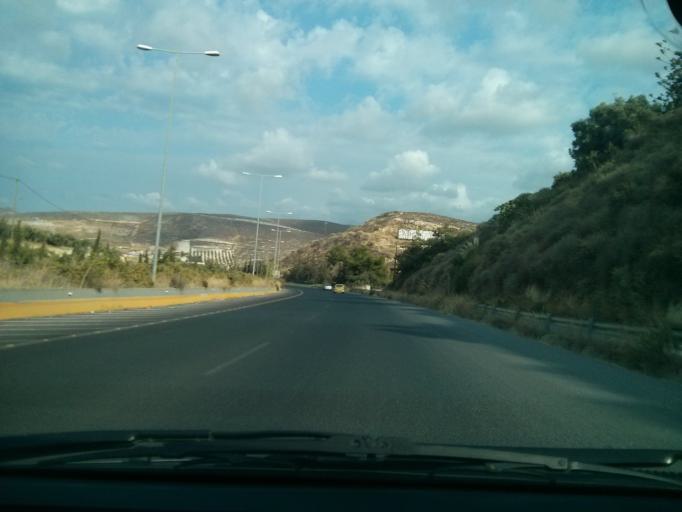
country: GR
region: Crete
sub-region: Nomos Irakleiou
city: Nea Alikarnassos
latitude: 35.3214
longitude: 25.1856
